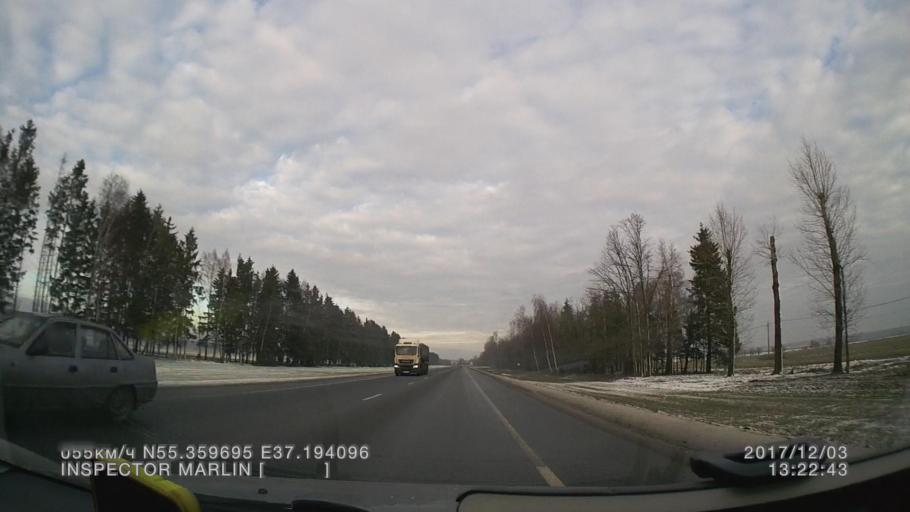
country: RU
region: Moskovskaya
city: Troitsk
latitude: 55.3597
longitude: 37.1942
